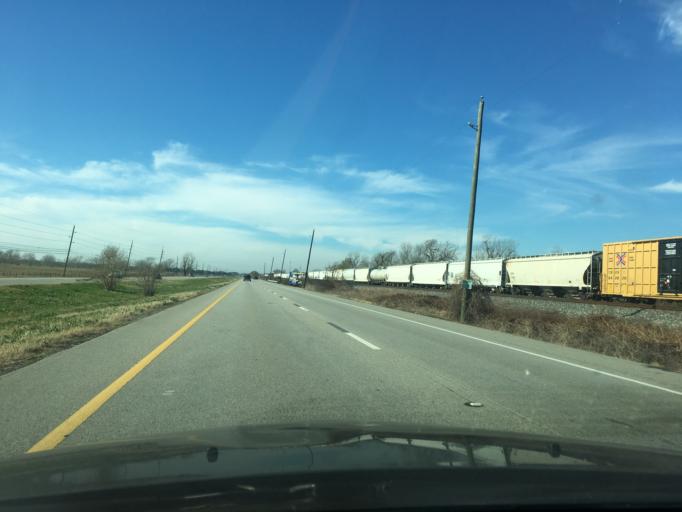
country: US
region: Texas
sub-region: Fort Bend County
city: New Territory
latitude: 29.6003
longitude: -95.7000
